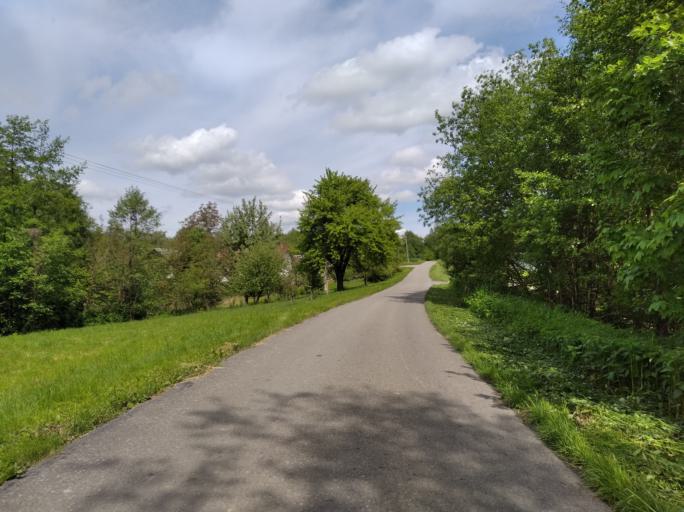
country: PL
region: Subcarpathian Voivodeship
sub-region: Powiat strzyzowski
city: Czudec
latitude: 49.9240
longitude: 21.8336
